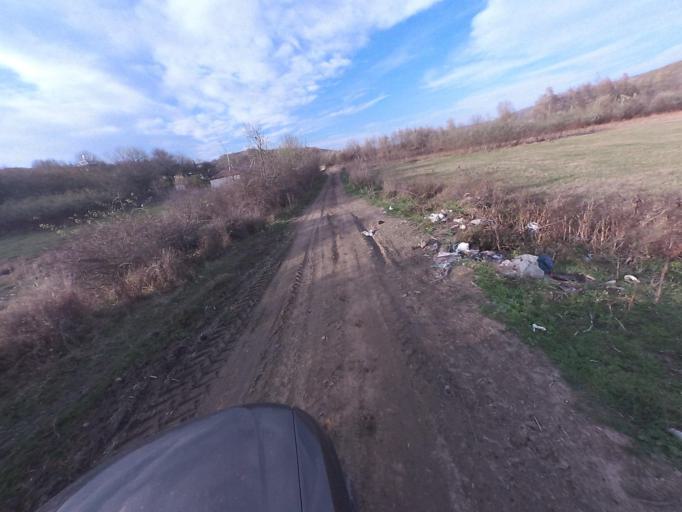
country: RO
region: Vaslui
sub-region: Comuna Gherghesti
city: Gherghesti
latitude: 46.4876
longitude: 27.5300
